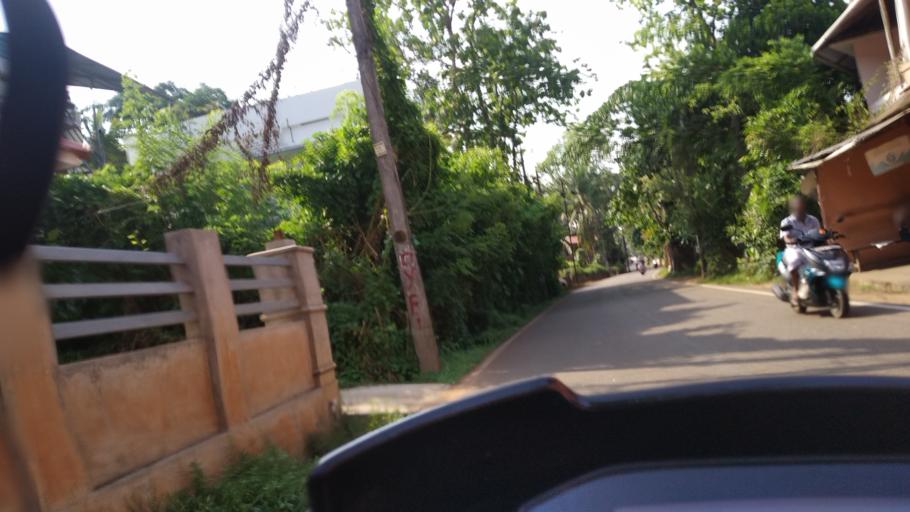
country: IN
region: Kerala
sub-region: Ernakulam
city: Piravam
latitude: 9.8710
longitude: 76.4992
